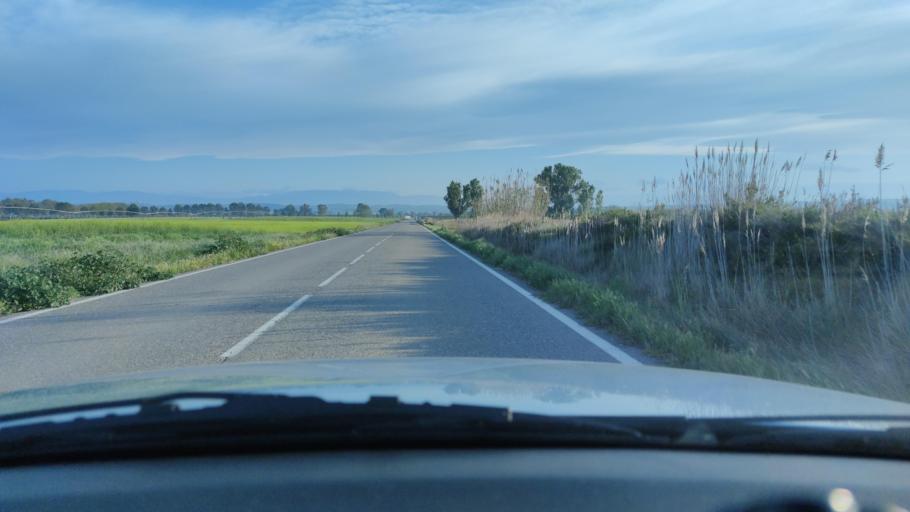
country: ES
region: Catalonia
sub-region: Provincia de Lleida
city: Ivars d'Urgell
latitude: 41.7132
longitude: 0.9824
